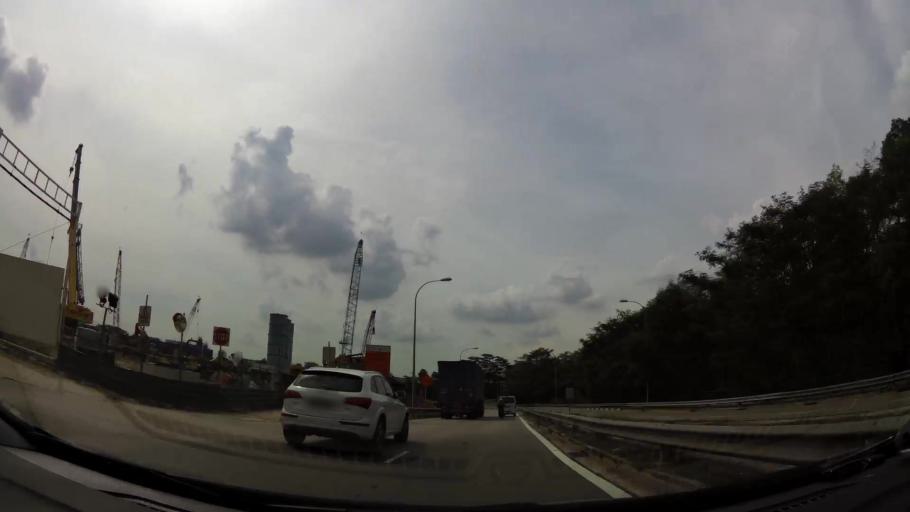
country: MY
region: Johor
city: Johor Bahru
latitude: 1.4511
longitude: 103.7856
